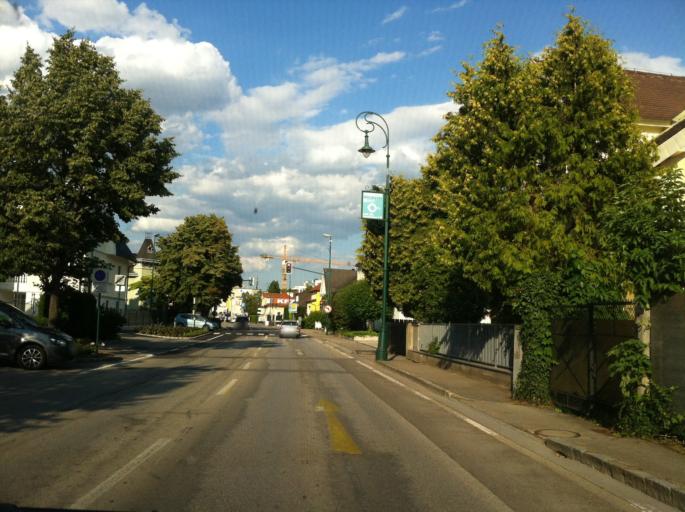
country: AT
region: Lower Austria
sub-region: Politischer Bezirk Tulln
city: Tulln
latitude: 48.3289
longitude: 16.0510
